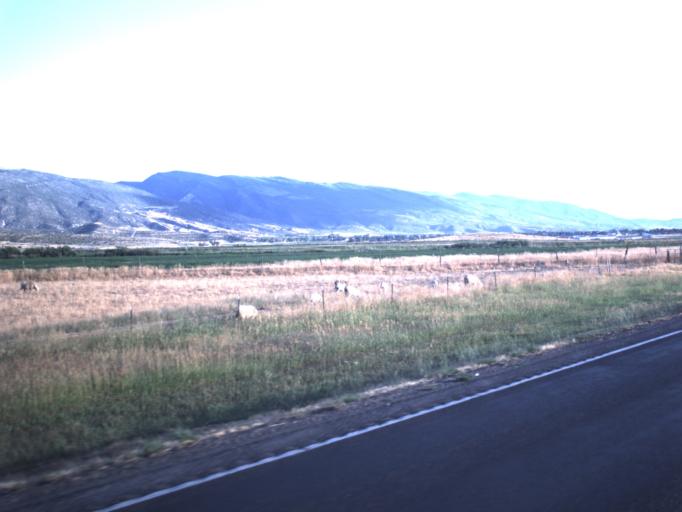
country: US
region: Utah
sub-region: Sanpete County
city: Ephraim
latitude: 39.3966
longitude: -111.5742
